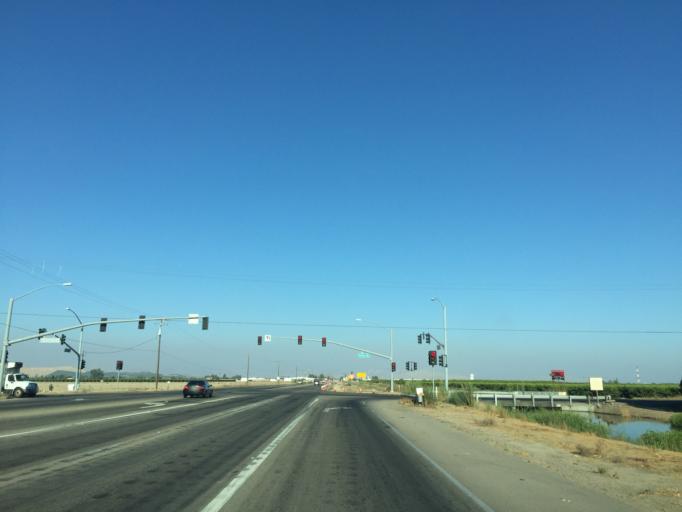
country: US
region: California
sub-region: Fresno County
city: Reedley
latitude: 36.5463
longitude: -119.4496
